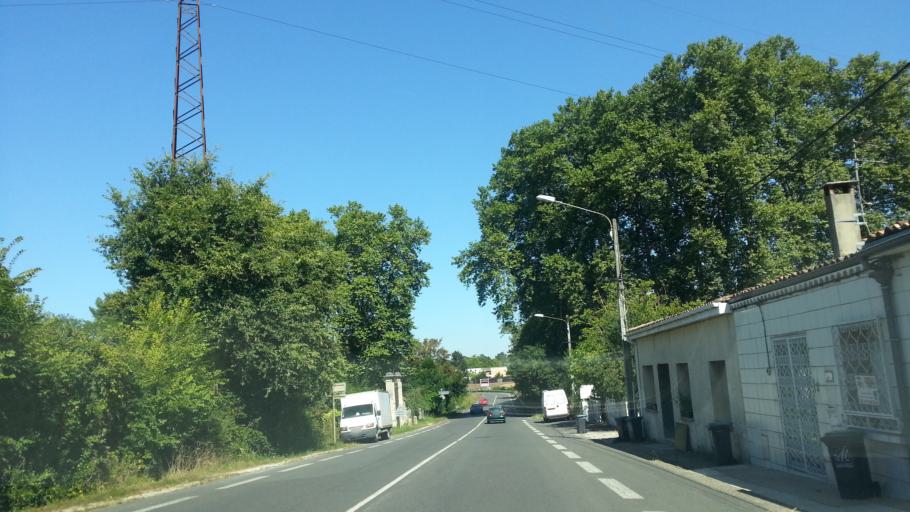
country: FR
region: Aquitaine
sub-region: Departement de la Gironde
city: Villenave-d'Ornon
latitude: 44.7570
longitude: -0.5528
